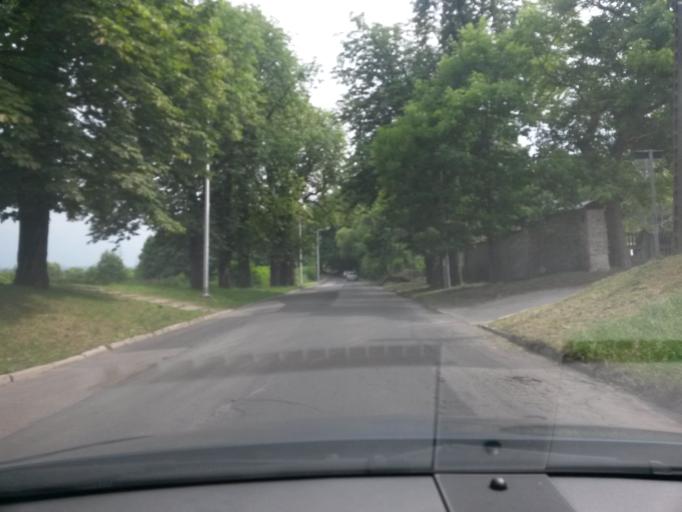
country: PL
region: Silesian Voivodeship
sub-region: Powiat czestochowski
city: Huta Stara B
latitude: 50.7634
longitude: 19.1544
